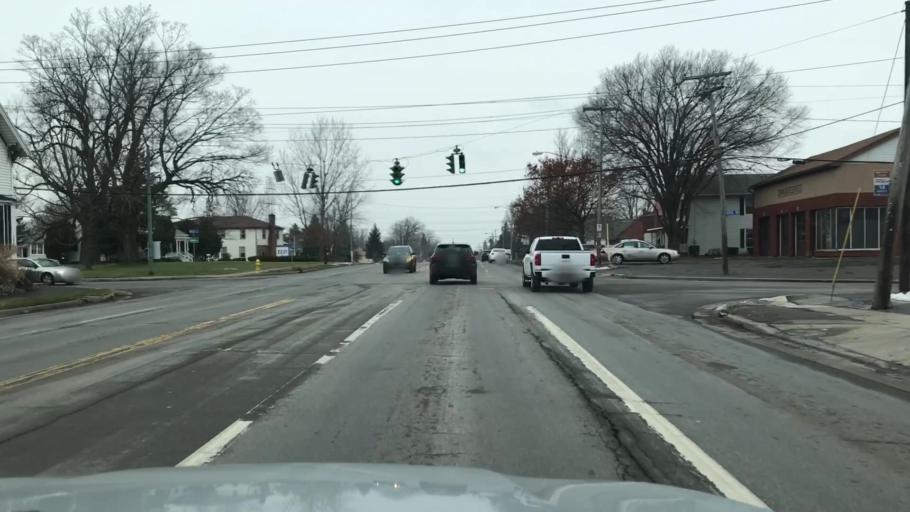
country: US
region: New York
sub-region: Erie County
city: Blasdell
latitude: 42.8042
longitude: -78.7972
